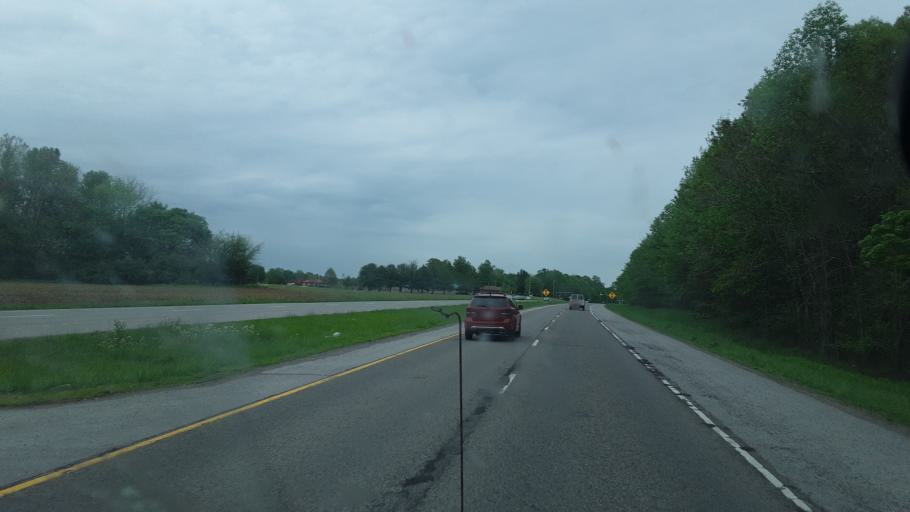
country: US
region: Illinois
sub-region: Jackson County
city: Murphysboro
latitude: 37.7659
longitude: -89.3029
